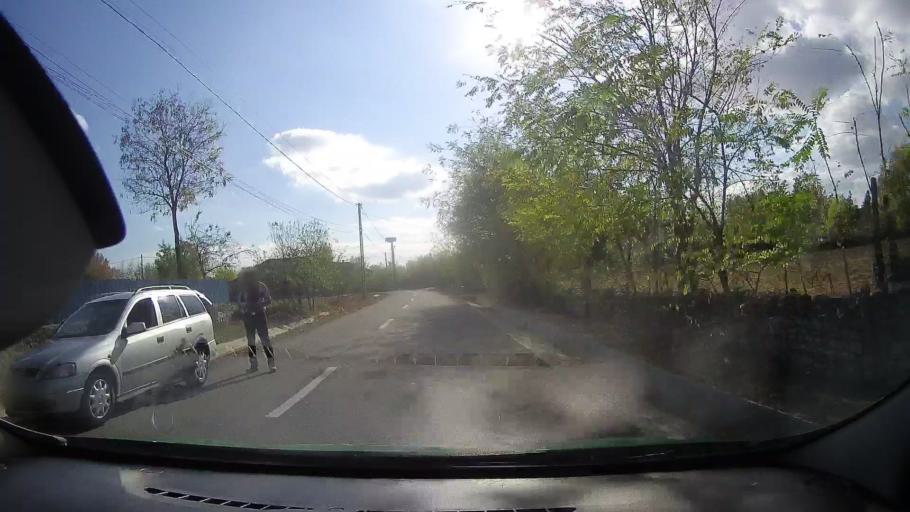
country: RO
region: Constanta
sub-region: Comuna Istria
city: Istria
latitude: 44.5740
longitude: 28.7140
